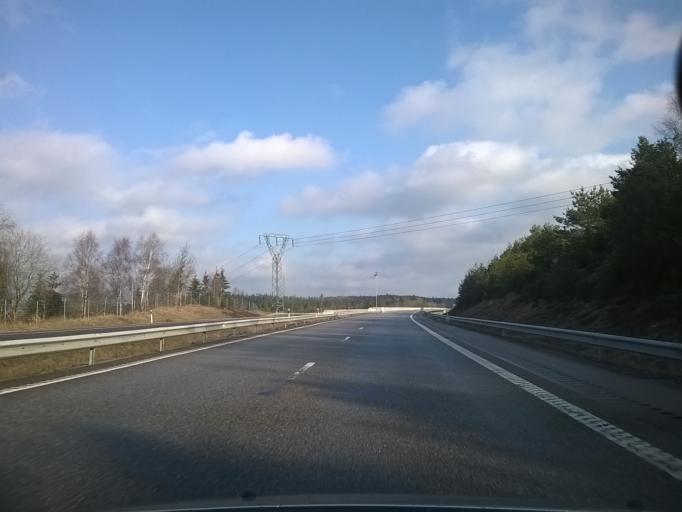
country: SE
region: Vaestra Goetaland
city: Svanesund
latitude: 58.1076
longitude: 11.8793
